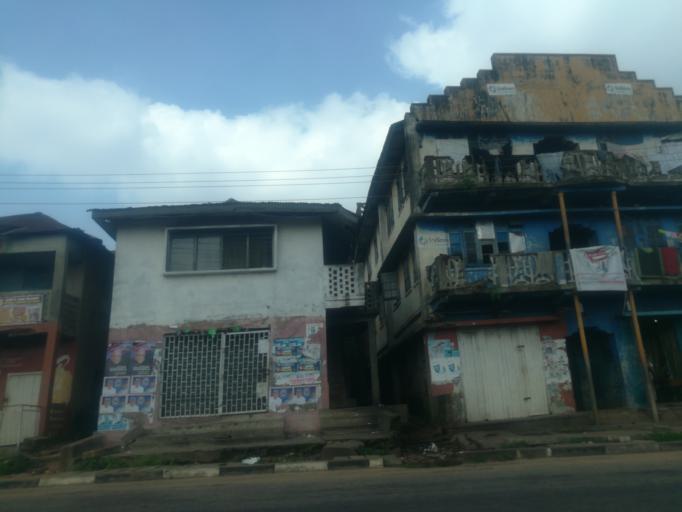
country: NG
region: Oyo
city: Ibadan
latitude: 7.3845
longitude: 3.8997
